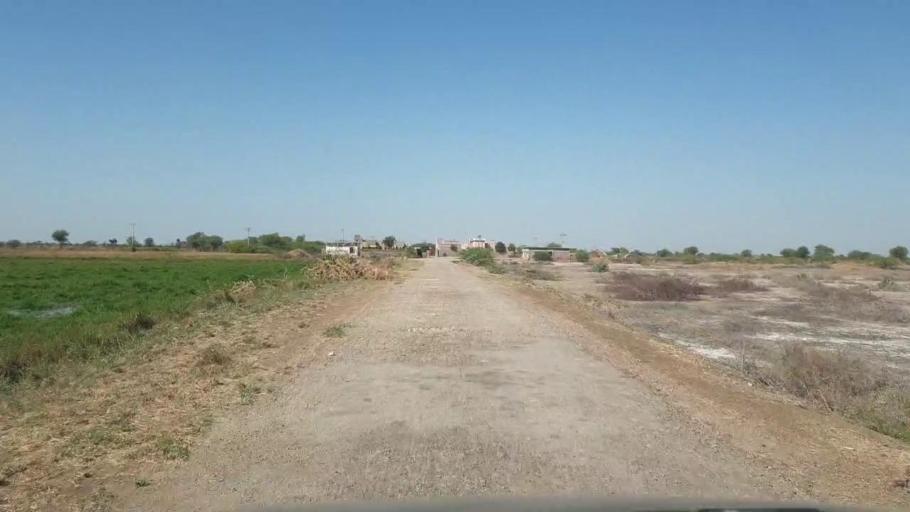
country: PK
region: Sindh
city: Dhoro Naro
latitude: 25.4017
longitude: 69.6185
